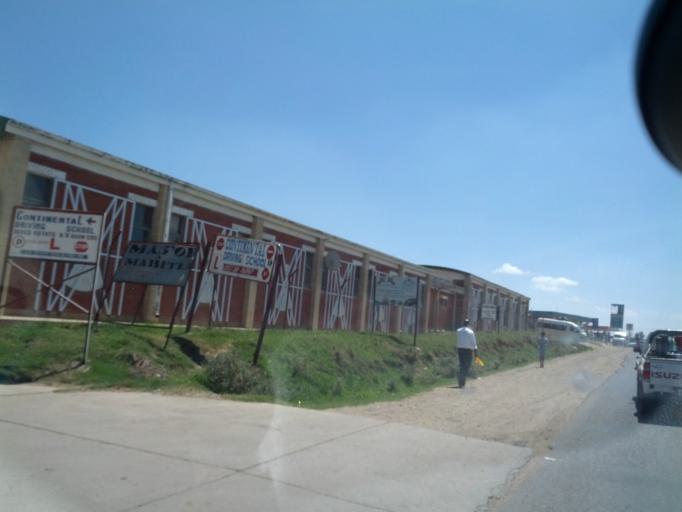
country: LS
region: Butha-Buthe
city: Butha-Buthe
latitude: -28.7695
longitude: 28.2481
